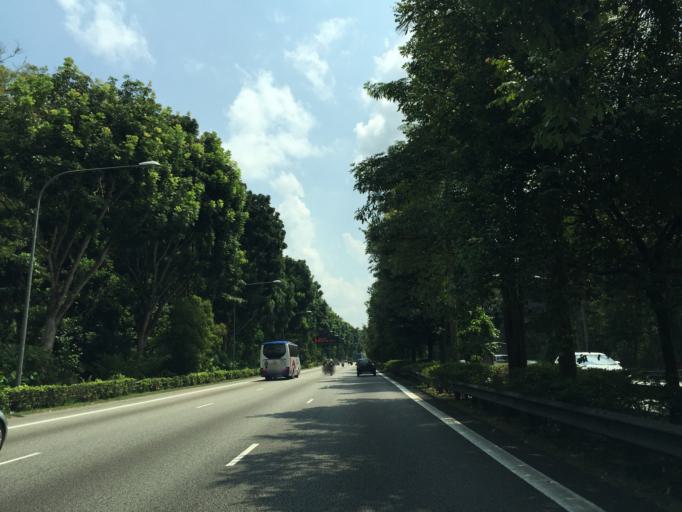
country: SG
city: Singapore
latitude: 1.3537
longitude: 103.7874
